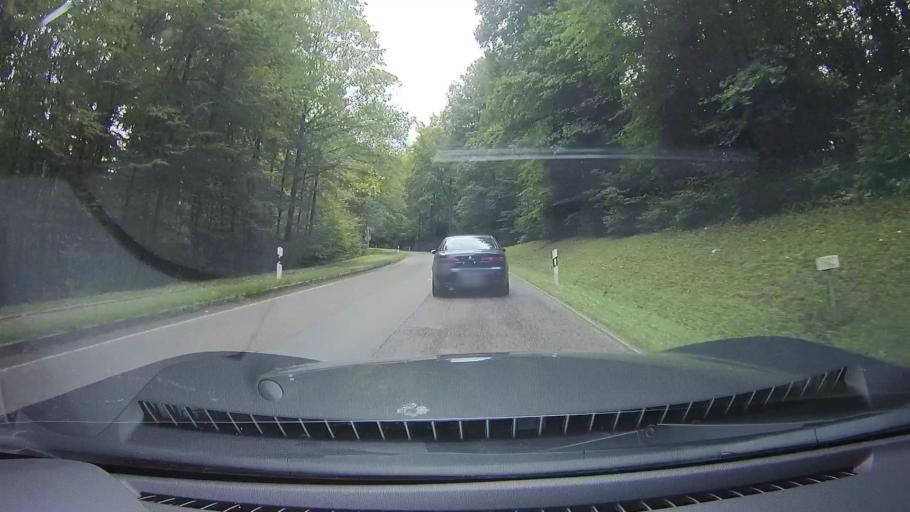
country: DE
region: Baden-Wuerttemberg
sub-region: Regierungsbezirk Stuttgart
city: Althutte
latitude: 48.9239
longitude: 9.5852
